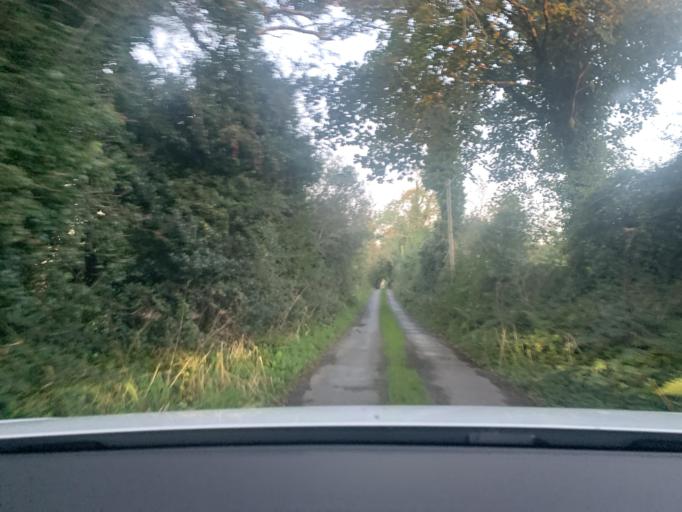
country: IE
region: Connaught
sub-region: Sligo
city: Sligo
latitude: 54.2750
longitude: -8.4195
